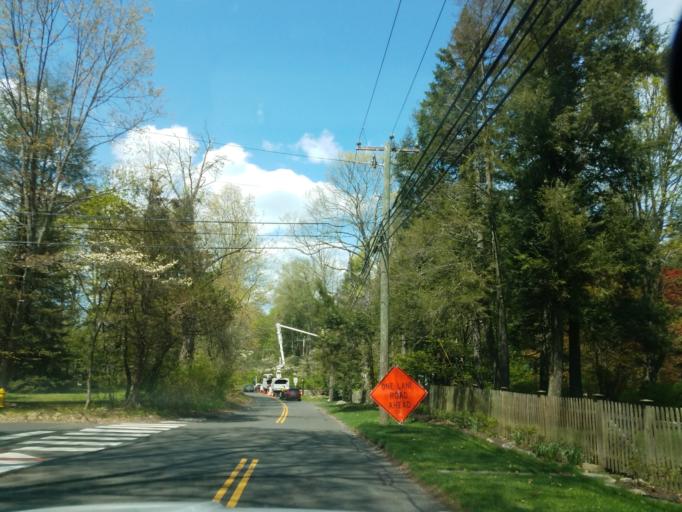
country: US
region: Connecticut
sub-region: Fairfield County
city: Norwalk
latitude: 41.1440
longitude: -73.4363
